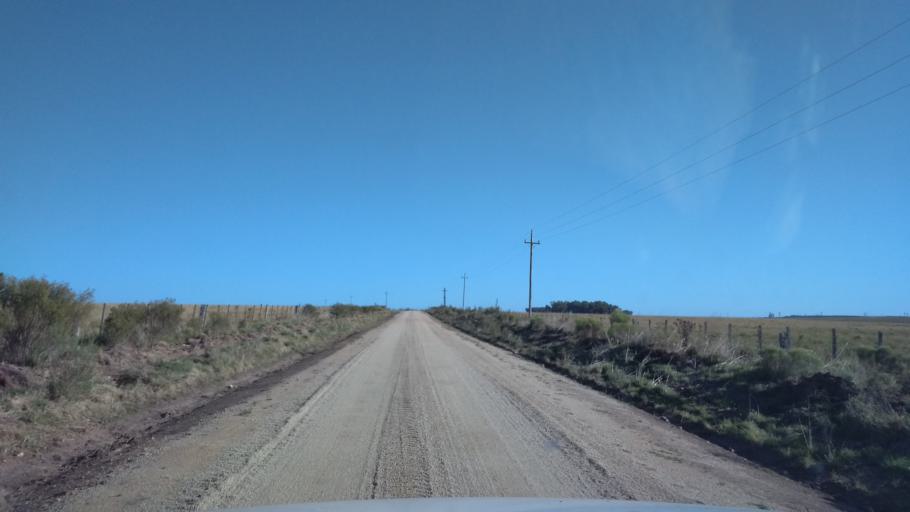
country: UY
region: Florida
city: Casupa
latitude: -34.0263
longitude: -55.7820
